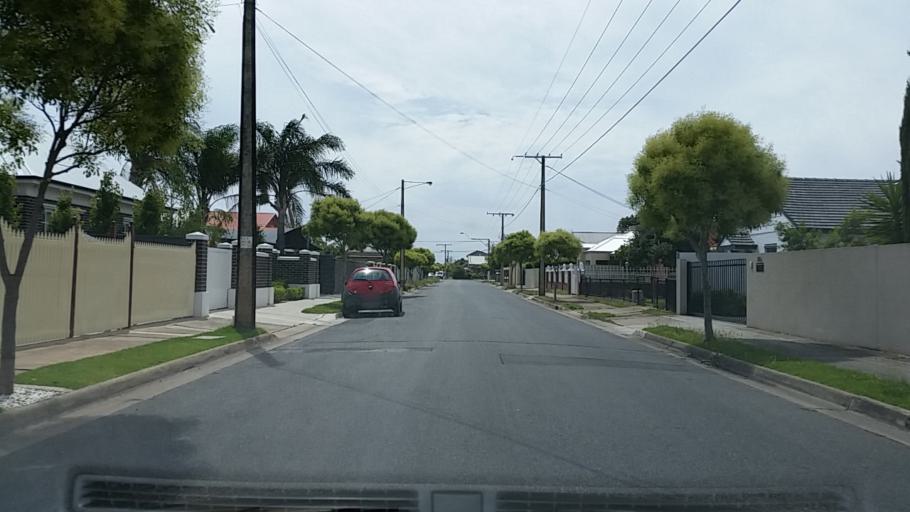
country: AU
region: South Australia
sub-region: Charles Sturt
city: Woodville
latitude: -34.8819
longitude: 138.5550
